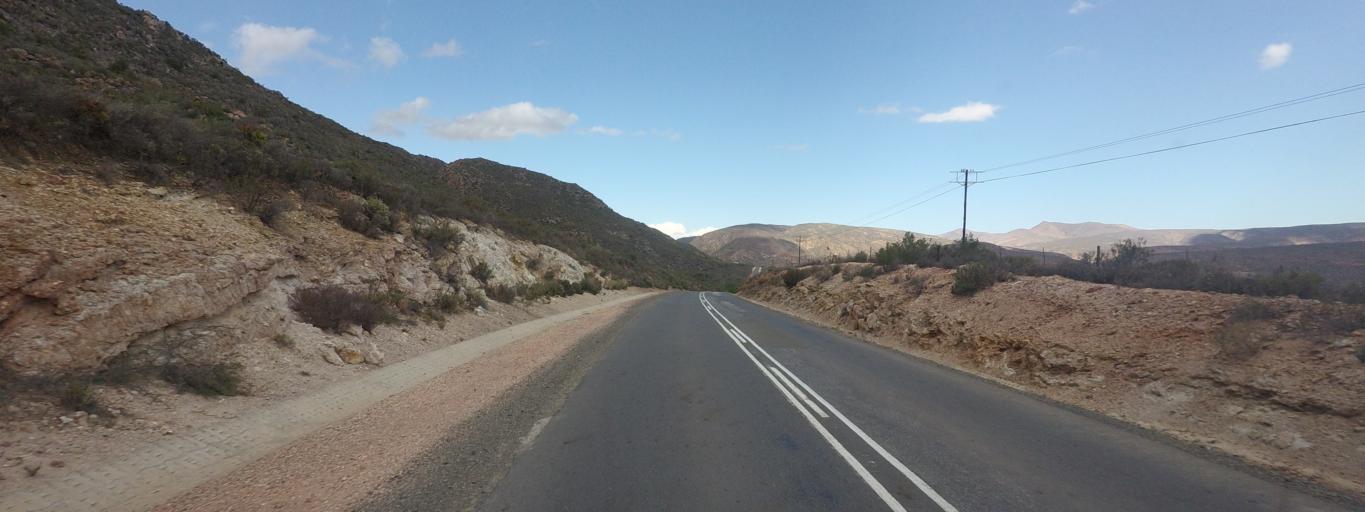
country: ZA
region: Western Cape
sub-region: Eden District Municipality
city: Ladismith
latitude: -33.4702
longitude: 21.4910
